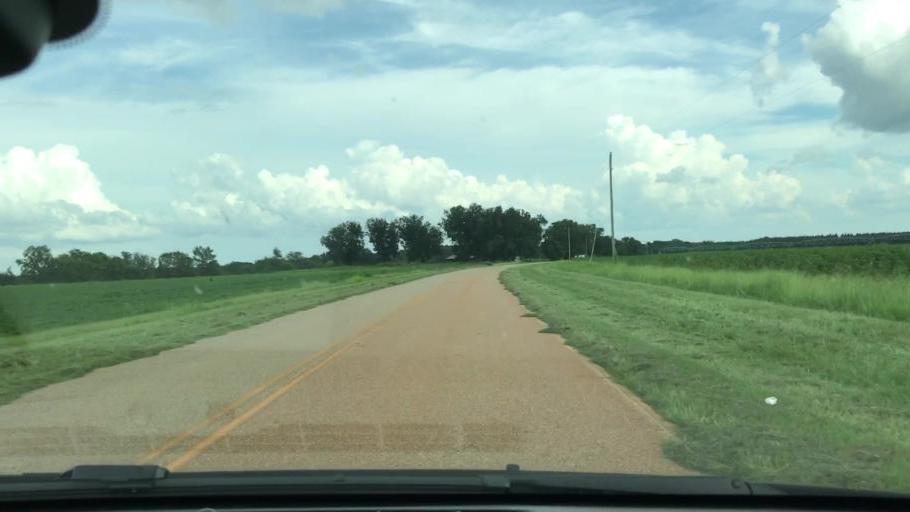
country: US
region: Georgia
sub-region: Clay County
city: Fort Gaines
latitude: 31.5683
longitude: -84.9930
